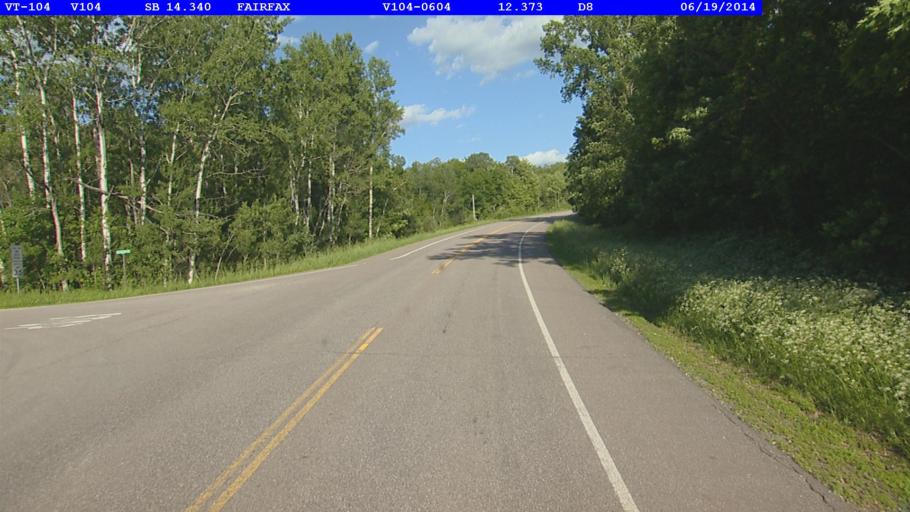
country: US
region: Vermont
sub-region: Franklin County
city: Saint Albans
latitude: 44.7606
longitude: -73.0608
